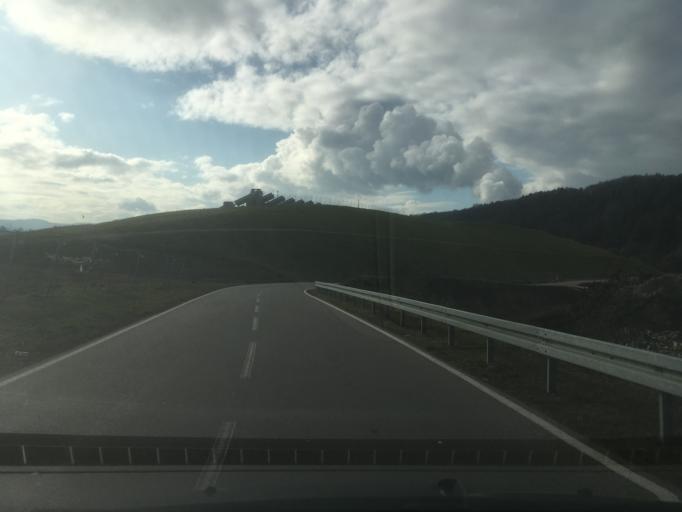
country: CH
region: Aargau
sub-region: Bezirk Zurzach
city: Koblenz
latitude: 47.6211
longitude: 8.2482
